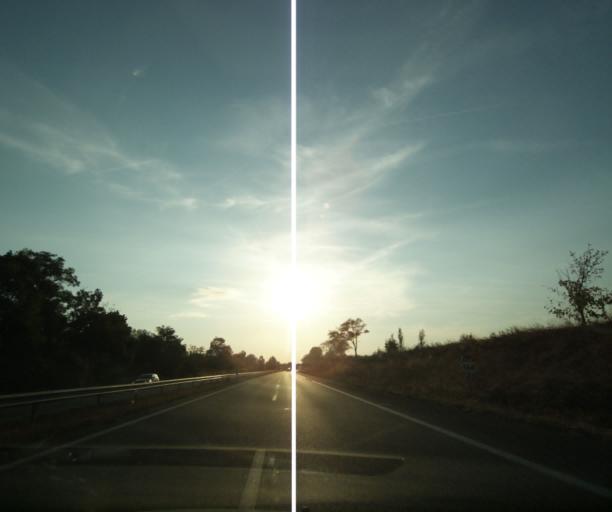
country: FR
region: Midi-Pyrenees
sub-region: Departement du Tarn-et-Garonne
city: Saint-Nicolas-de-la-Grave
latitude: 44.0404
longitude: 1.0415
